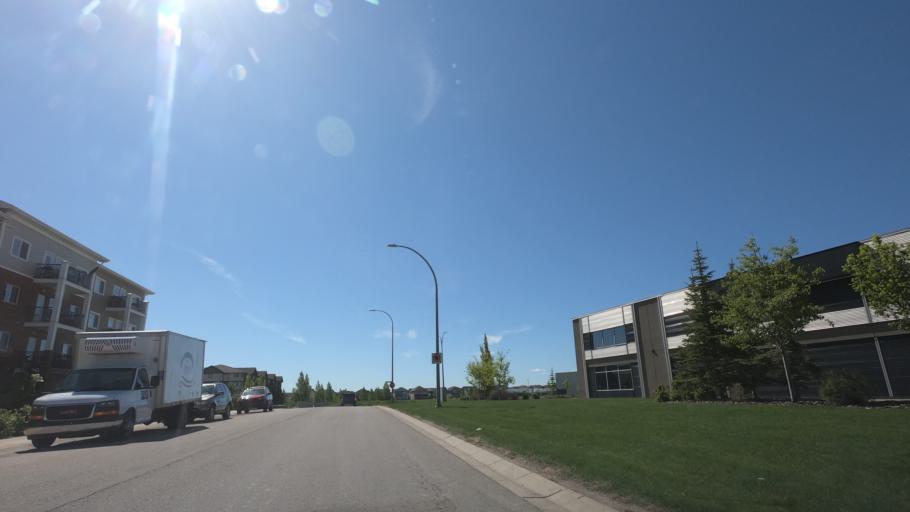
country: CA
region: Alberta
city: Airdrie
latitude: 51.2667
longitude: -113.9942
